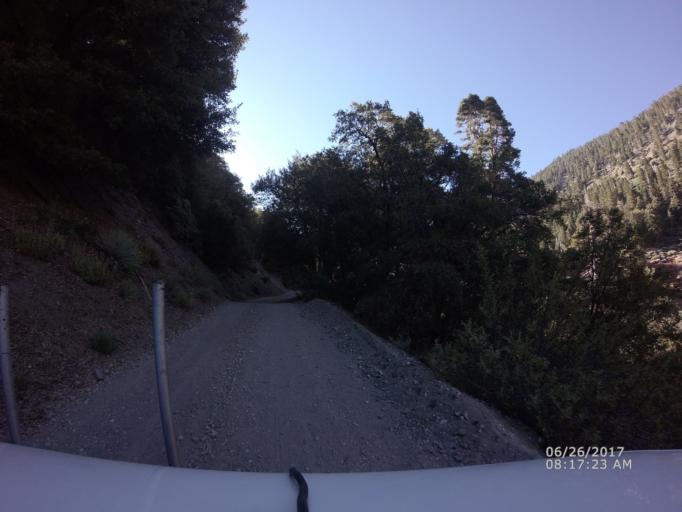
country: US
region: California
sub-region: San Bernardino County
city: Pinon Hills
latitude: 34.3780
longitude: -117.7611
